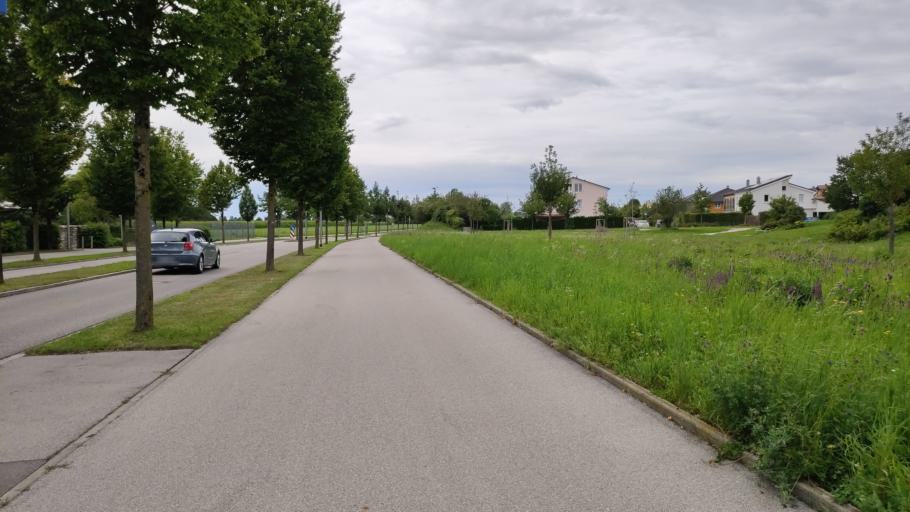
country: DE
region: Bavaria
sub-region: Swabia
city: Konigsbrunn
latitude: 48.2648
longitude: 10.8823
